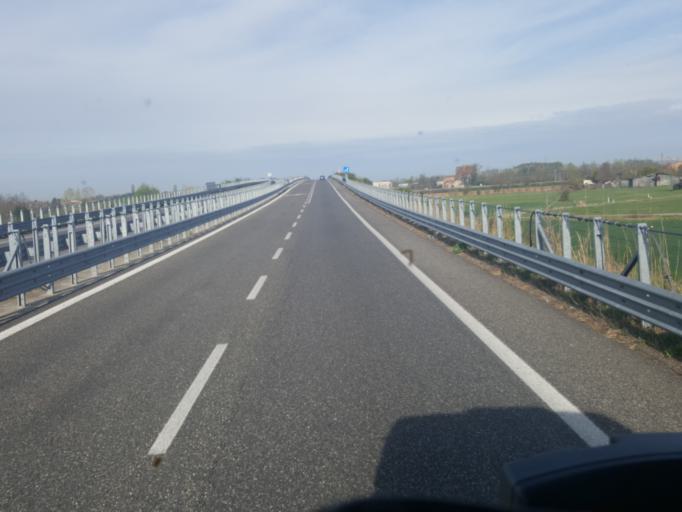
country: IT
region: Piedmont
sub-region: Provincia di Alessandria
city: Alessandria
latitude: 44.9342
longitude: 8.5964
